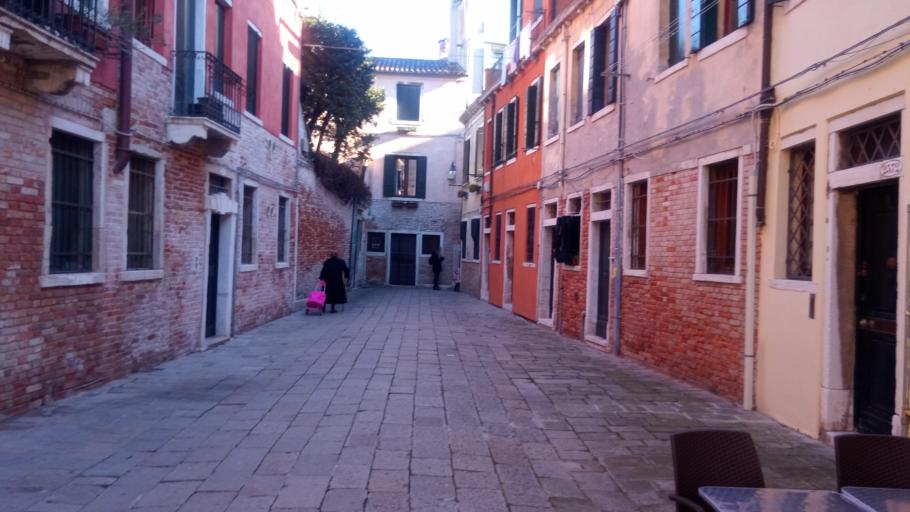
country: IT
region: Veneto
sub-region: Provincia di Venezia
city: Venice
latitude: 45.4384
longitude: 12.3264
